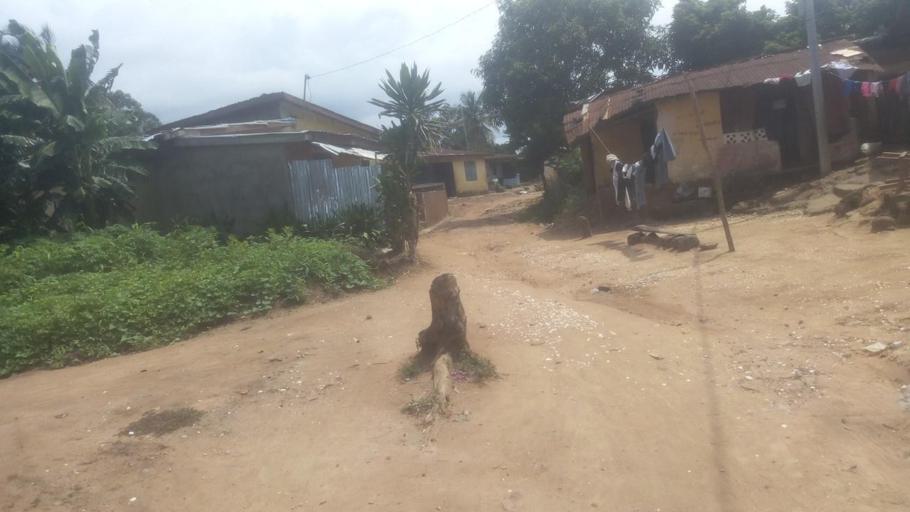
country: SL
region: Western Area
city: Freetown
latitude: 8.5242
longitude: -13.1486
